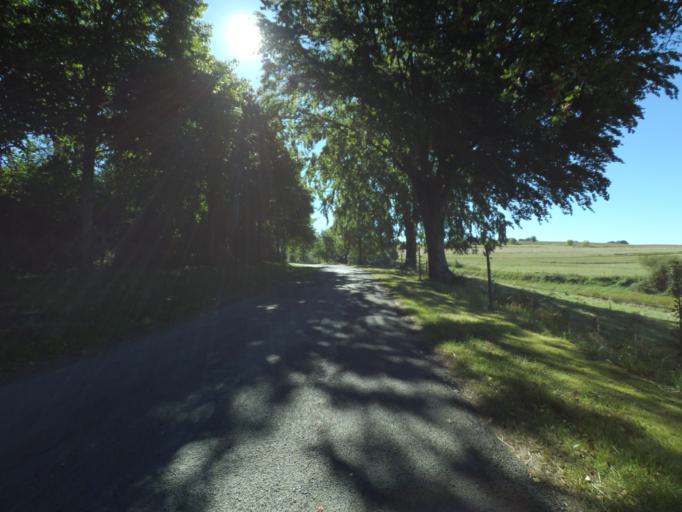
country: DE
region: Rheinland-Pfalz
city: Horscheid
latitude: 50.2038
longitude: 6.8516
